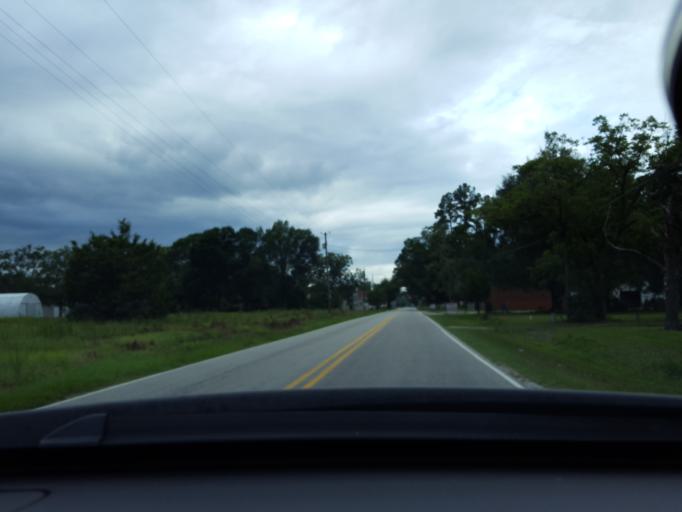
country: US
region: North Carolina
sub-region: Sampson County
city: Roseboro
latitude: 34.7831
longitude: -78.3916
